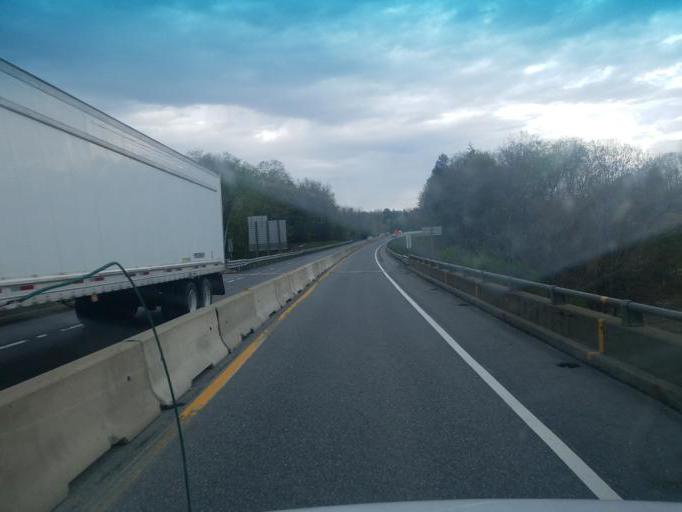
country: US
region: Maine
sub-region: Somerset County
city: Pittsfield
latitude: 44.8019
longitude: -69.3909
